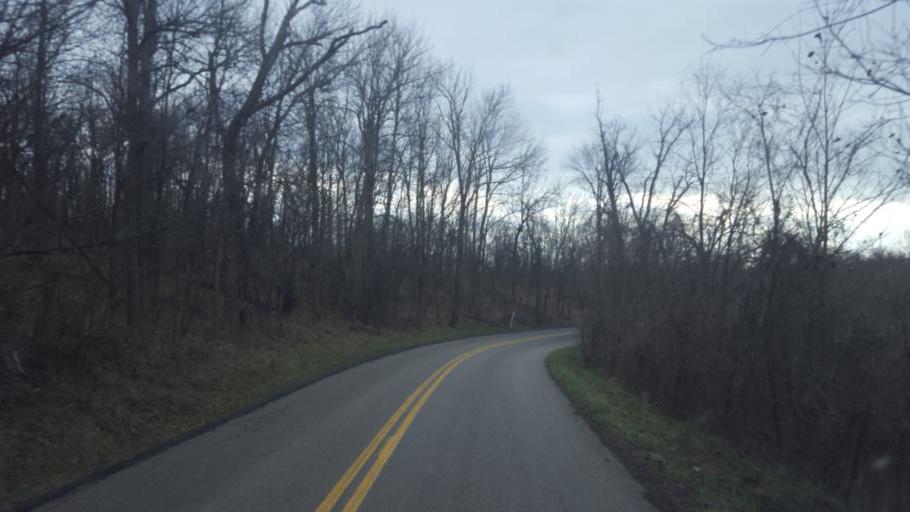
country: US
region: Ohio
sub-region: Gallia County
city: Gallipolis
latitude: 38.7128
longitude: -82.3392
